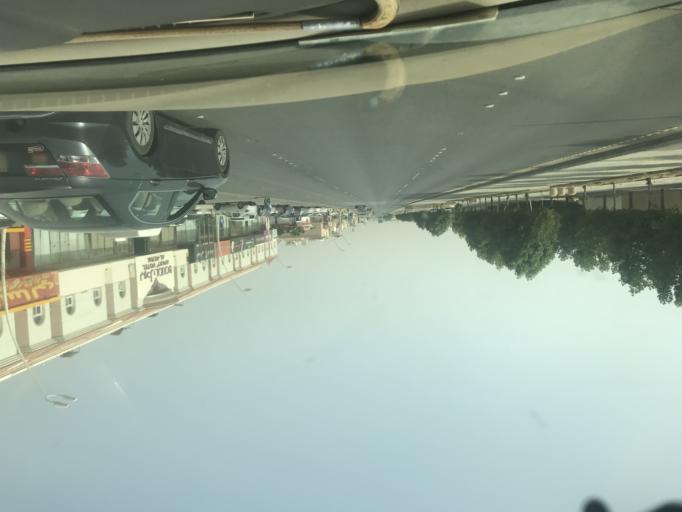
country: SA
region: Ar Riyad
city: Riyadh
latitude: 24.6775
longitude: 46.8010
